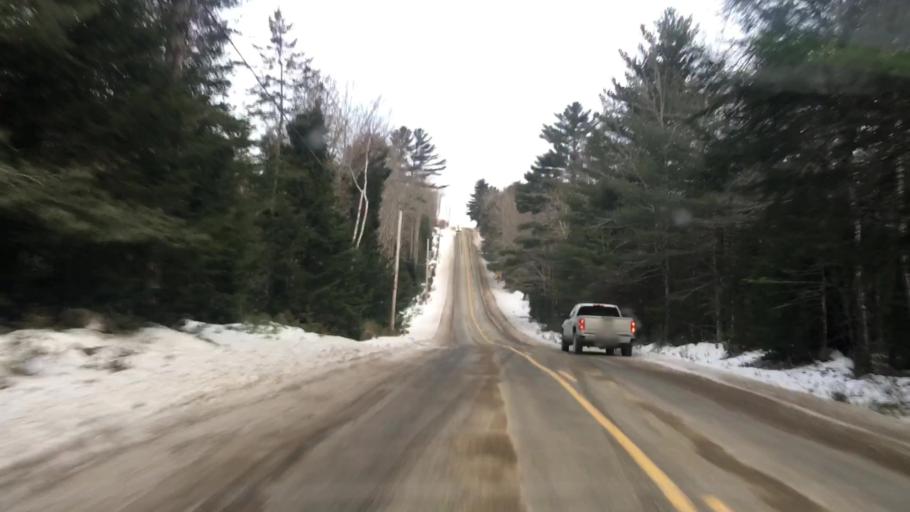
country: US
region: Maine
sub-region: Hancock County
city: Franklin
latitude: 44.8408
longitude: -68.3243
